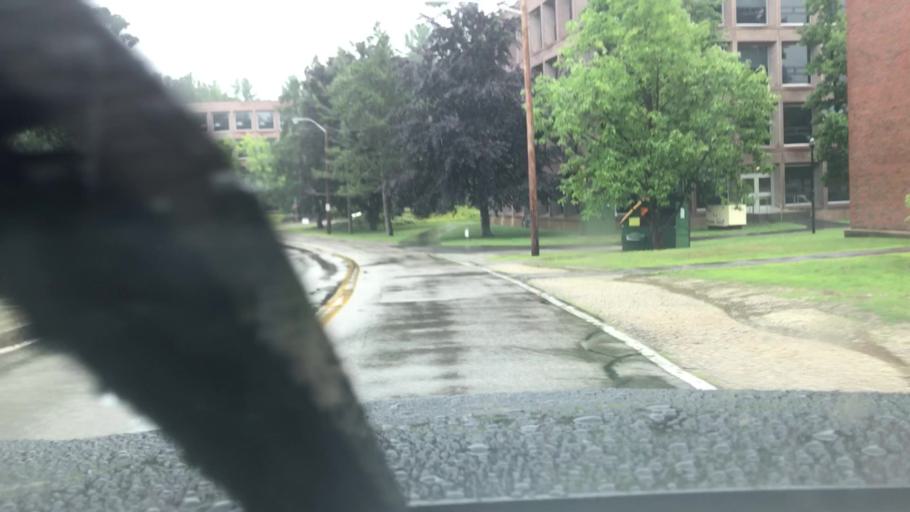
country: US
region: New Hampshire
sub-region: Strafford County
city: Durham
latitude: 43.1325
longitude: -70.9331
